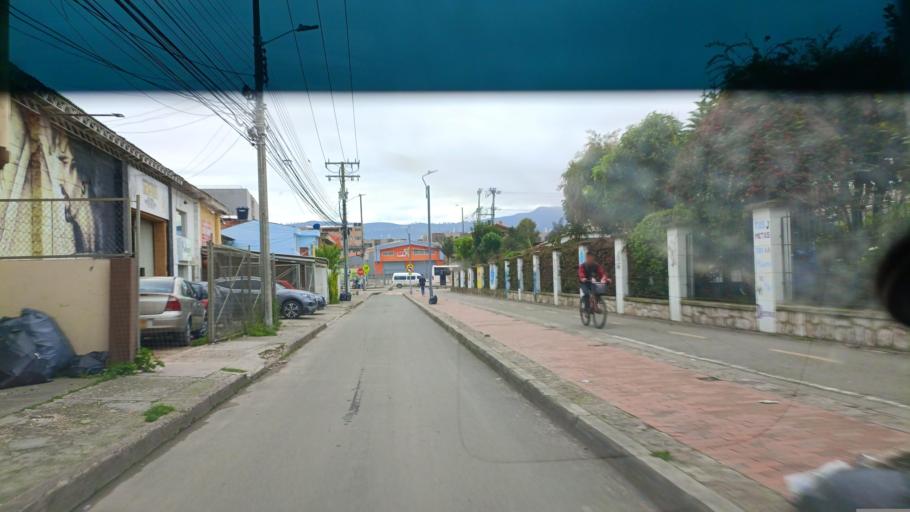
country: CO
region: Cundinamarca
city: Cajica
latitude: 4.9159
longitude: -74.0282
